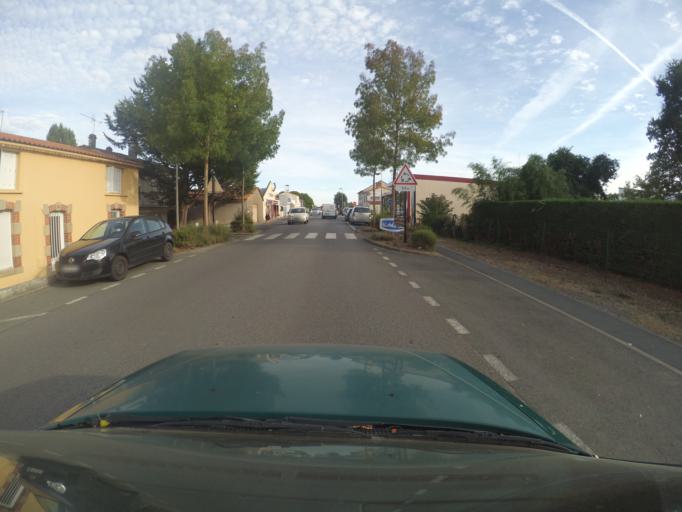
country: FR
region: Pays de la Loire
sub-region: Departement de la Vendee
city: Saint-Hilaire-de-Loulay
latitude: 47.0051
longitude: -1.3343
